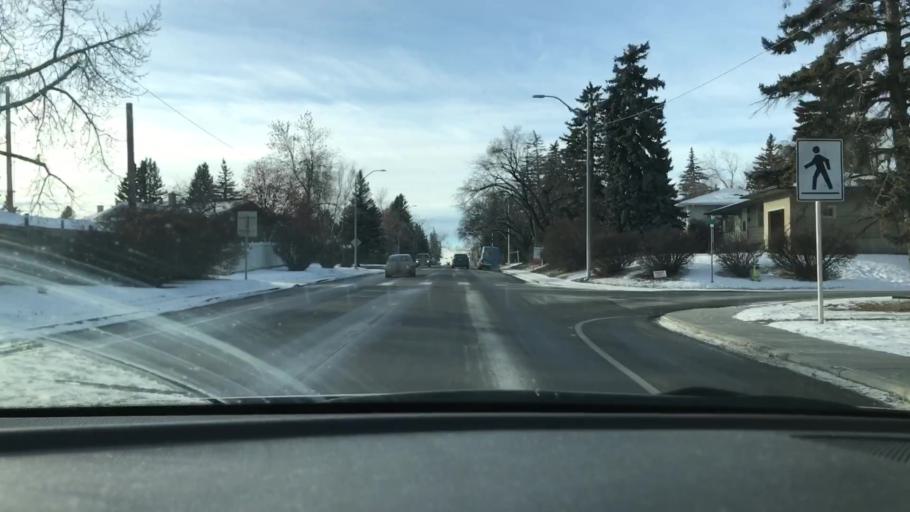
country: CA
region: Alberta
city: Calgary
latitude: 51.0245
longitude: -114.1343
